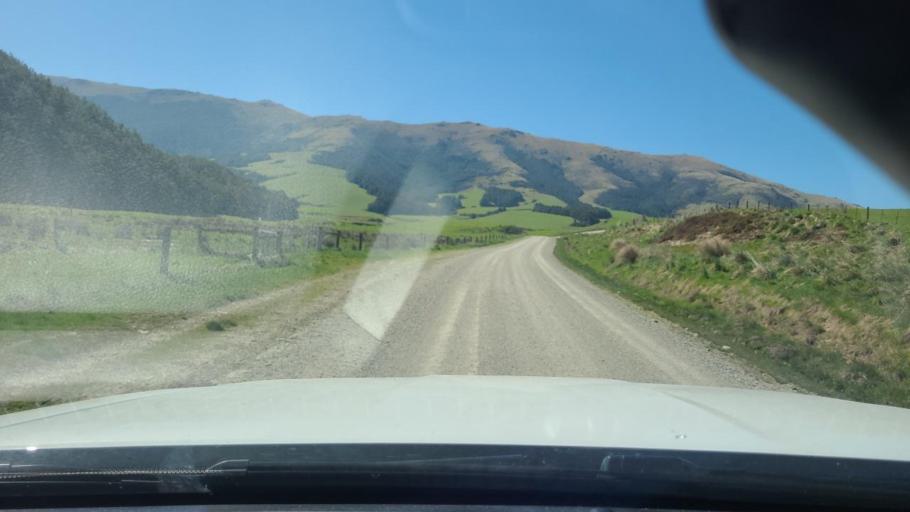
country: NZ
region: Southland
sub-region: Gore District
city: Gore
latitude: -45.7573
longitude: 168.9495
